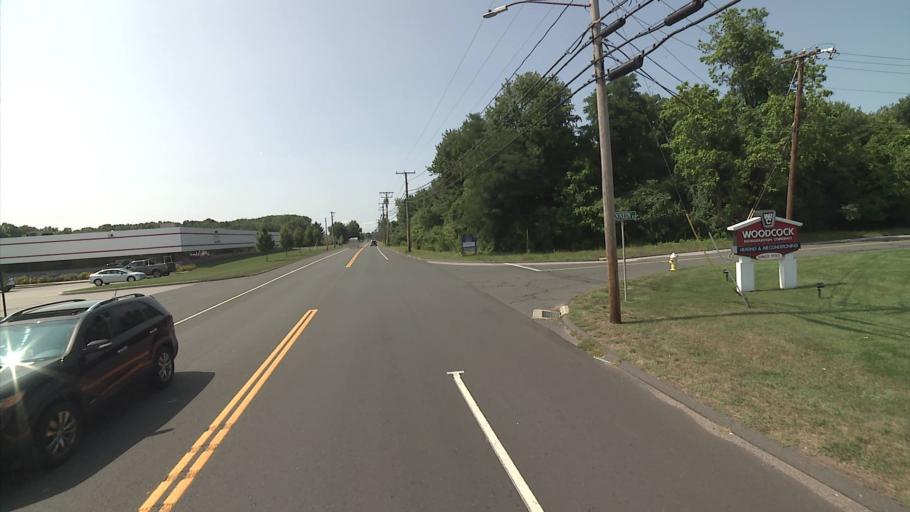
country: US
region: Connecticut
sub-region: Hartford County
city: South Windsor
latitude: 41.8533
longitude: -72.5866
